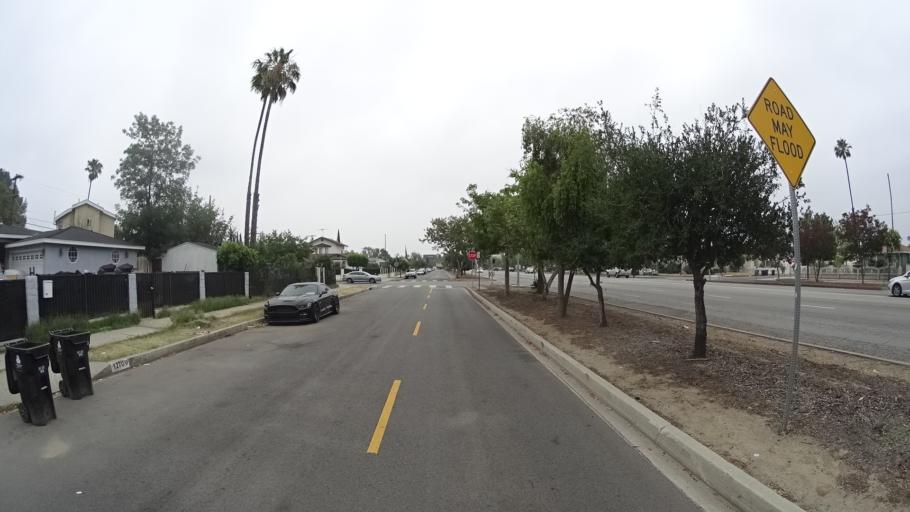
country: US
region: California
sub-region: Los Angeles County
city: North Hollywood
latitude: 34.1868
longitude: -118.4101
